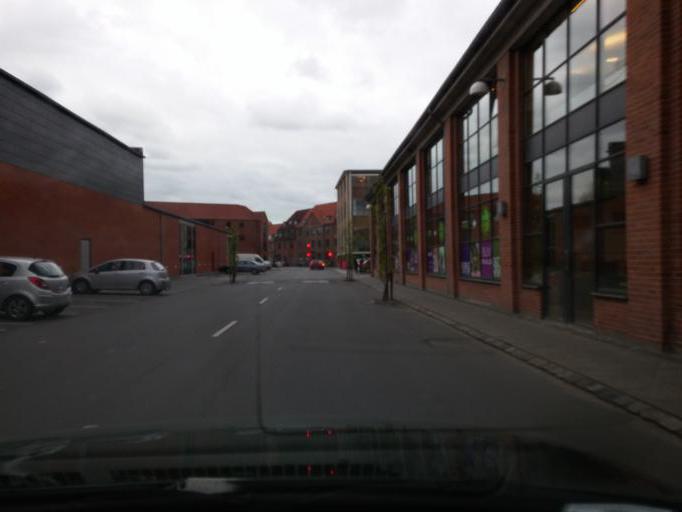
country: DK
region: South Denmark
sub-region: Odense Kommune
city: Odense
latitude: 55.4052
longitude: 10.3911
